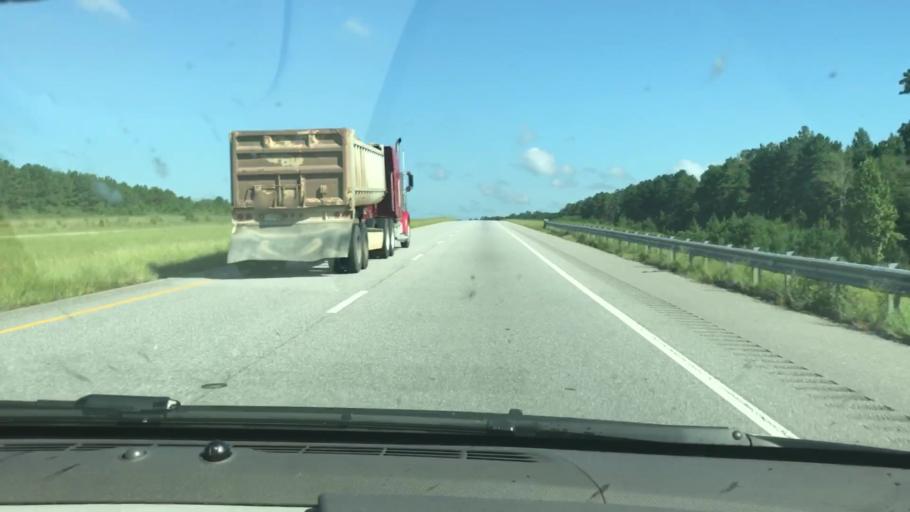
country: US
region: Alabama
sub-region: Barbour County
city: Eufaula
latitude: 32.1192
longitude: -85.1513
